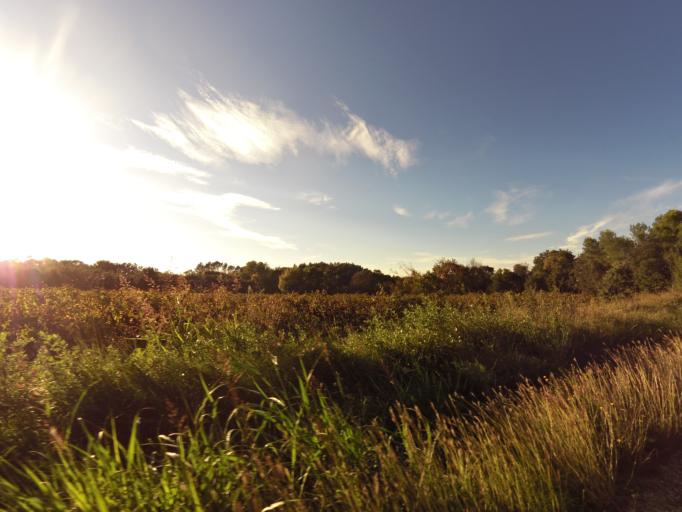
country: FR
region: Languedoc-Roussillon
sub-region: Departement du Gard
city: Villevieille
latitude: 43.7996
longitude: 4.1192
